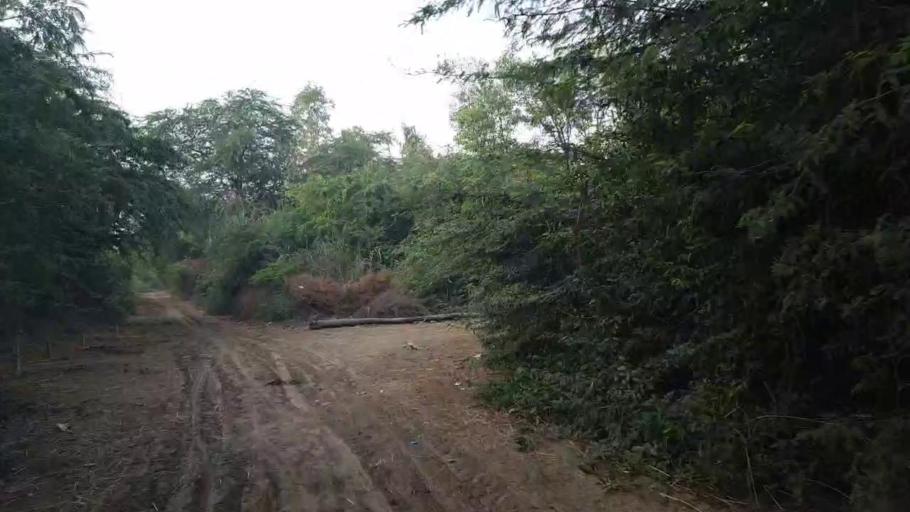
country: PK
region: Sindh
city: Tando Bago
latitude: 24.7801
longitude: 68.8764
